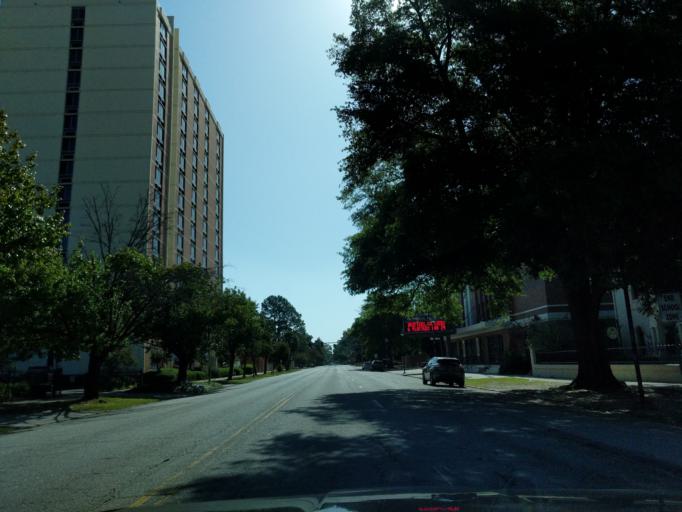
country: US
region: Georgia
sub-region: Richmond County
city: Augusta
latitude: 33.4719
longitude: -81.9665
